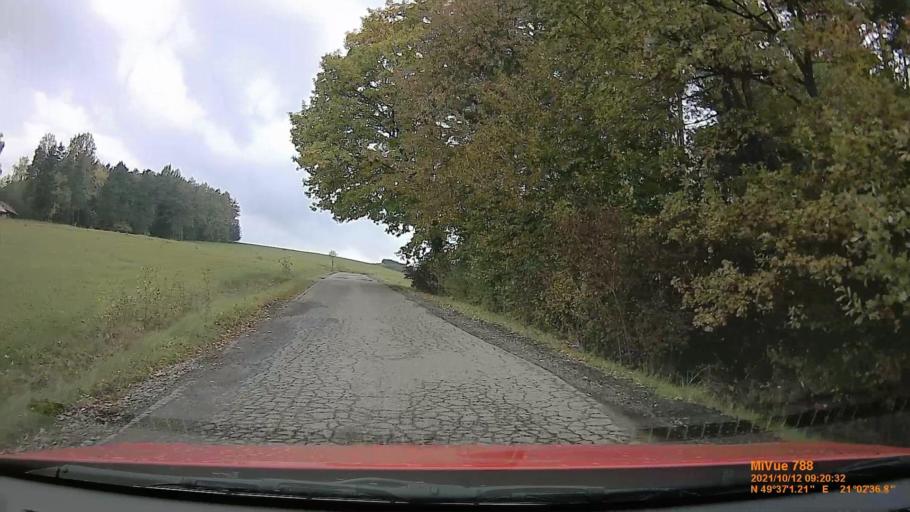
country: PL
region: Lesser Poland Voivodeship
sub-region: Powiat gorlicki
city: Ropa
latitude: 49.6171
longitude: 21.0433
